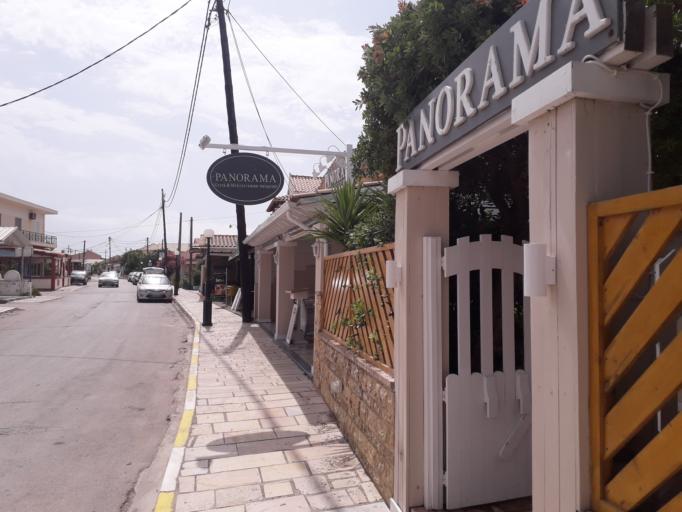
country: GR
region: Ionian Islands
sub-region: Nomos Kerkyras
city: Perivoli
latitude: 39.4262
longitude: 19.9447
